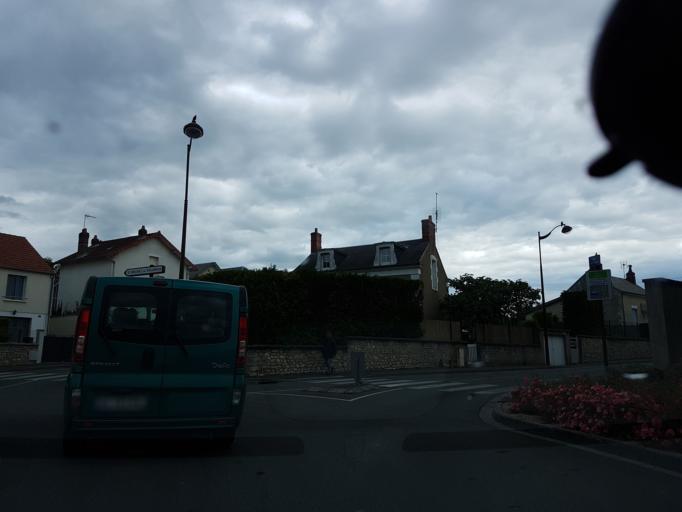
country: FR
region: Centre
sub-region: Departement du Cher
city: Bourges
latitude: 47.0956
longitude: 2.4078
